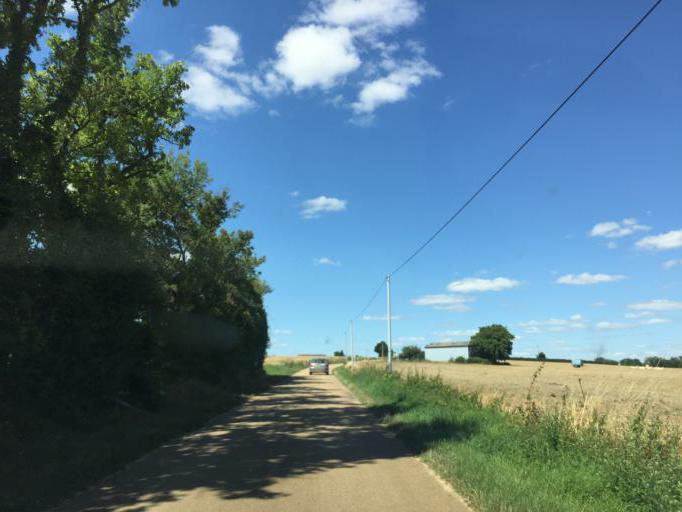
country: FR
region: Bourgogne
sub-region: Departement de l'Yonne
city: Fontenailles
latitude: 47.5688
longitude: 3.3441
